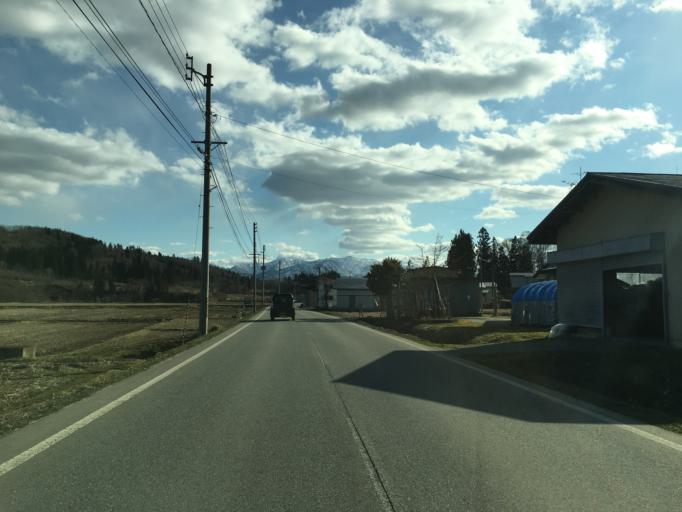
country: JP
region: Yamagata
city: Nagai
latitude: 37.9756
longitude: 139.9984
